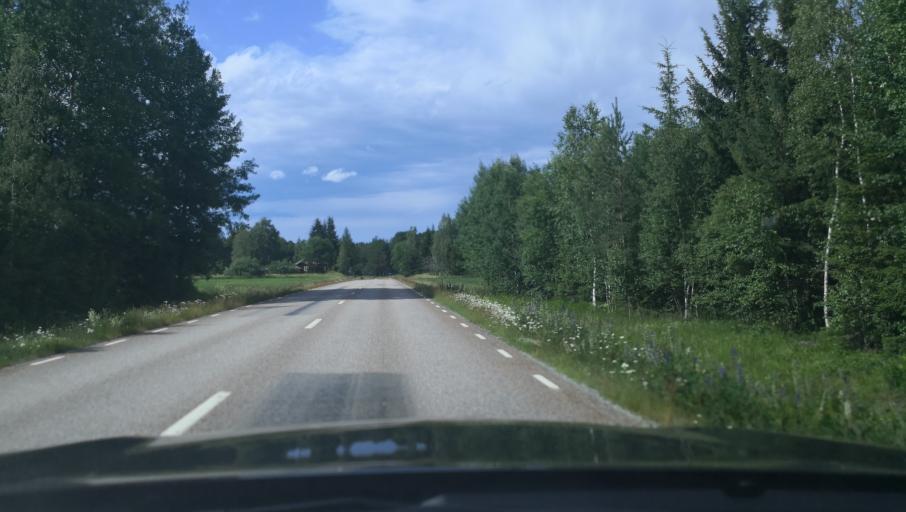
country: SE
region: Dalarna
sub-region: Avesta Kommun
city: Avesta
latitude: 59.9601
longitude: 16.2140
